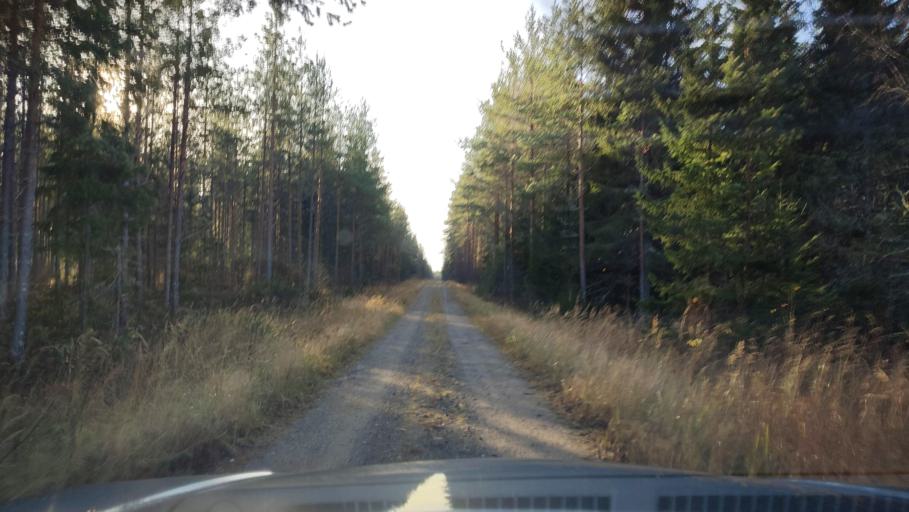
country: FI
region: Southern Ostrobothnia
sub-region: Suupohja
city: Karijoki
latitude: 62.1889
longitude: 21.6073
